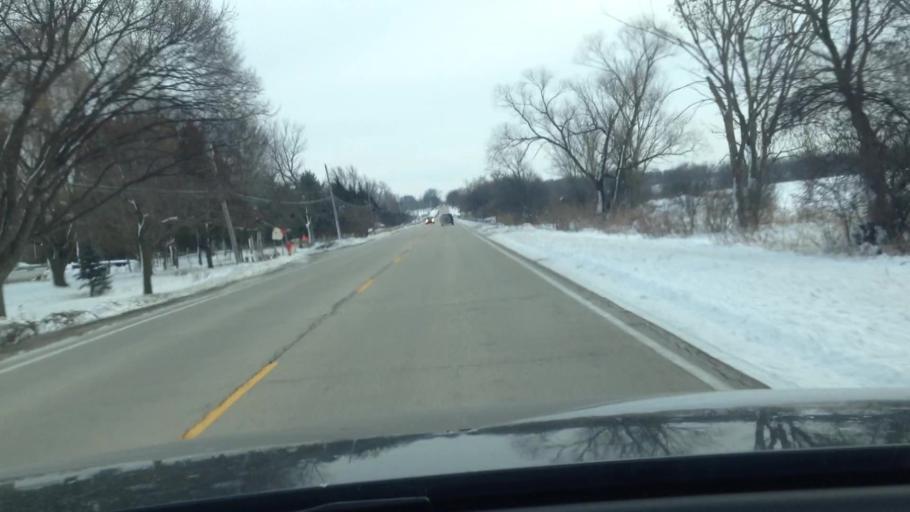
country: US
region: Illinois
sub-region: McHenry County
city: Woodstock
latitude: 42.3729
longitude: -88.4432
